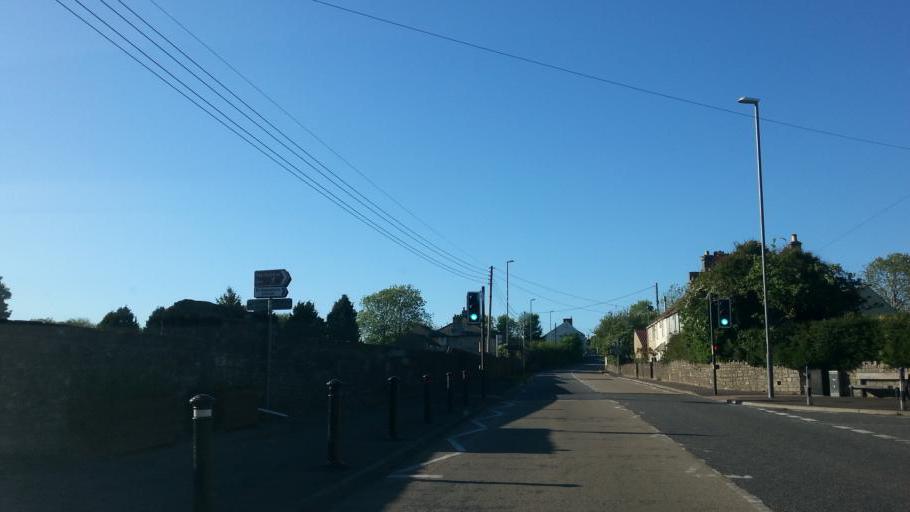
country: GB
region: England
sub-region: Bath and North East Somerset
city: Clutton
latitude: 51.3299
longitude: -2.5476
